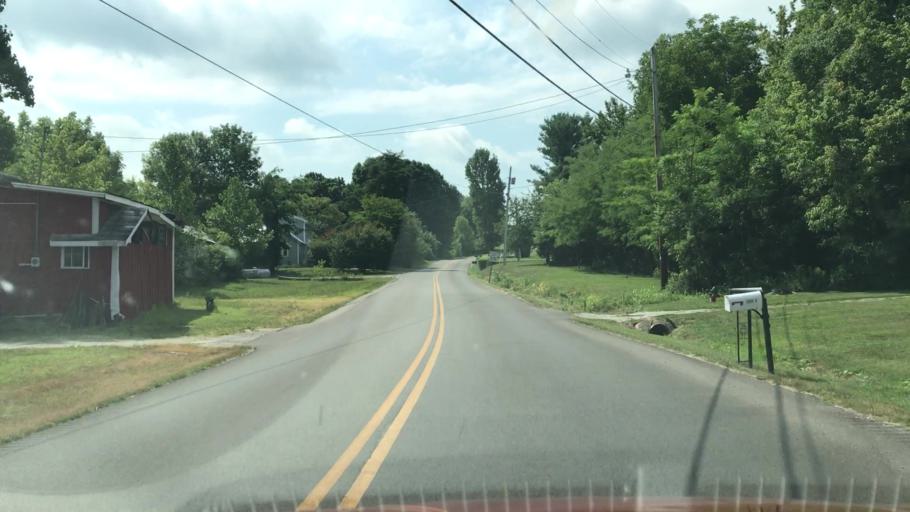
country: US
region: Kentucky
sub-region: Barren County
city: Glasgow
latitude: 36.9856
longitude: -85.9049
